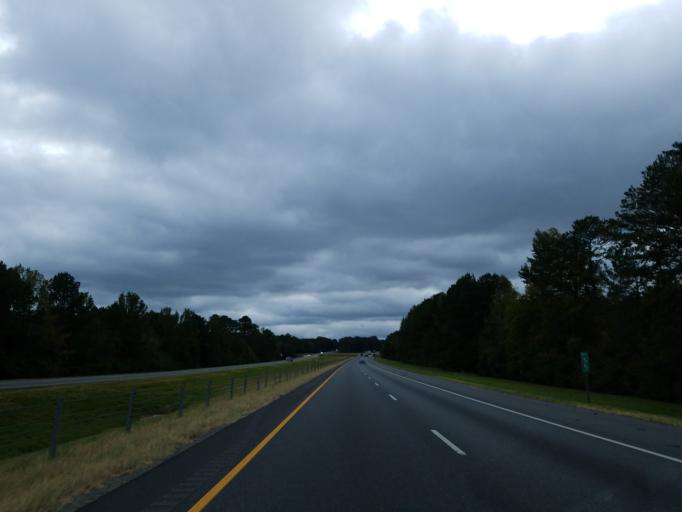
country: US
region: Alabama
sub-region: Hale County
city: Moundville
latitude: 33.0145
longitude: -87.7551
